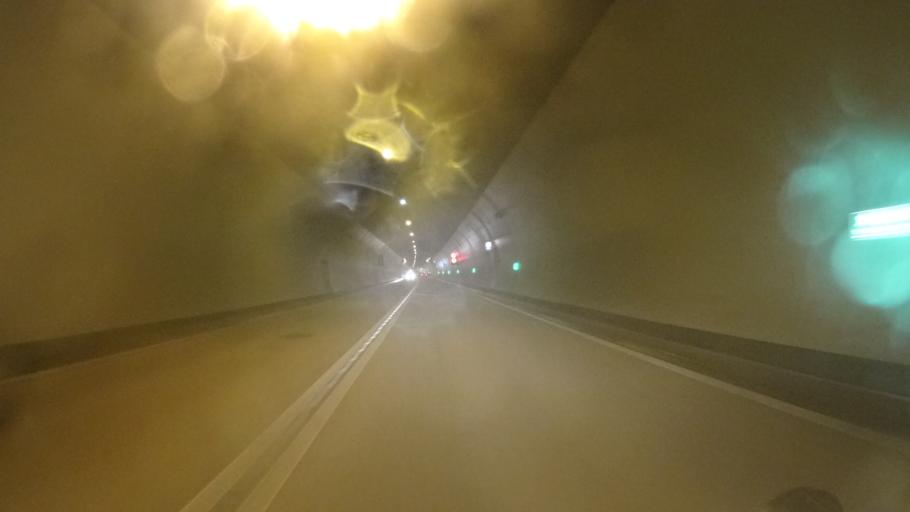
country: AT
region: Tyrol
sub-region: Politischer Bezirk Reutte
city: Vils
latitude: 47.5663
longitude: 10.6586
